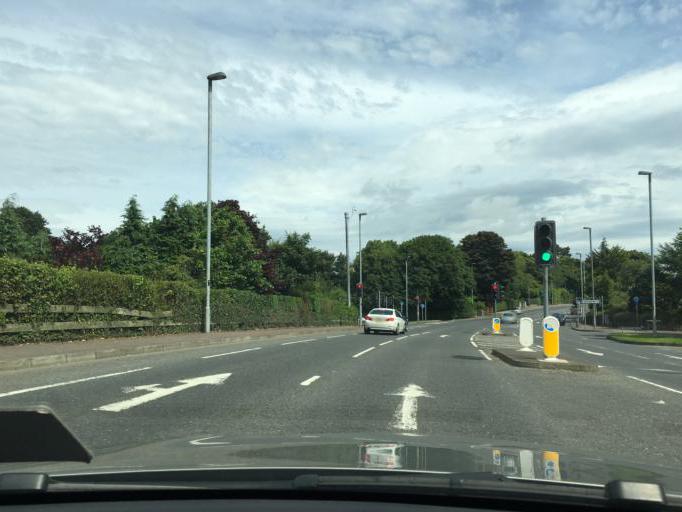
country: GB
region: Northern Ireland
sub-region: City of Derry
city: Derry
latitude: 55.0216
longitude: -7.3082
